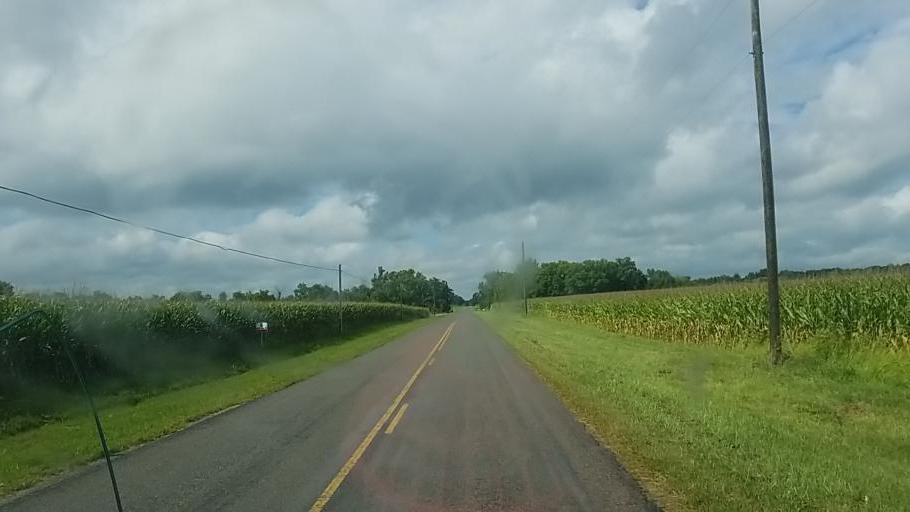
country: US
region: Ohio
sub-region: Hardin County
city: Kenton
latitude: 40.4959
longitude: -83.5191
